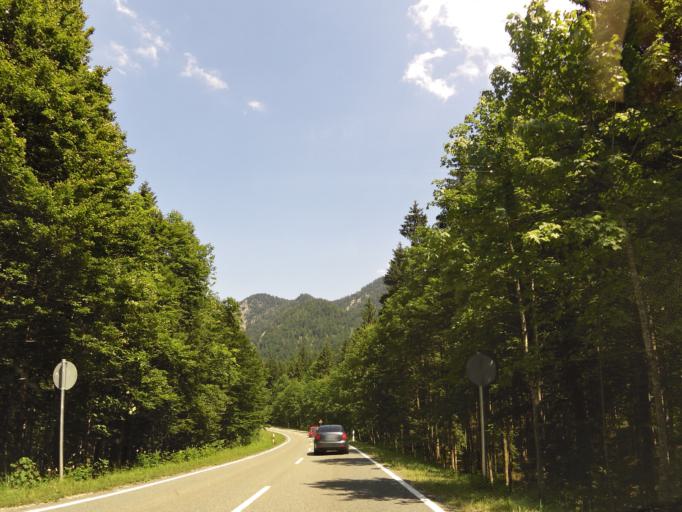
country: DE
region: Bavaria
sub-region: Upper Bavaria
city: Ruhpolding
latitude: 47.6915
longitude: 12.5969
